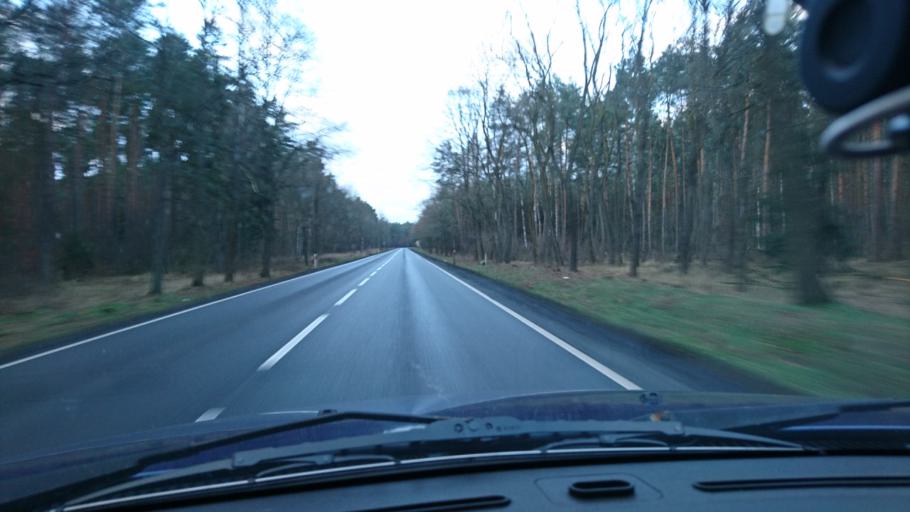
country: PL
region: Greater Poland Voivodeship
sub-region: Powiat kepinski
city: Kepno
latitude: 51.3340
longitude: 17.9565
